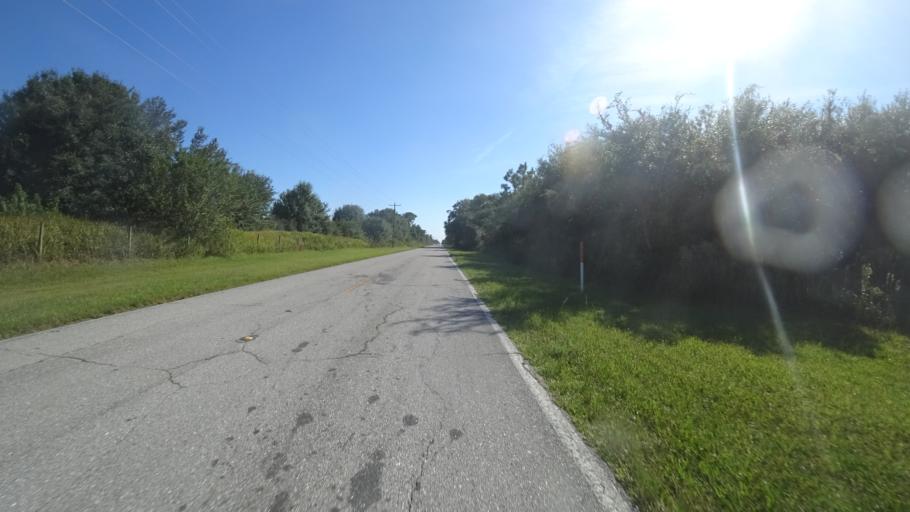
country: US
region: Florida
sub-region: Sarasota County
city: The Meadows
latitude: 27.4324
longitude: -82.2707
